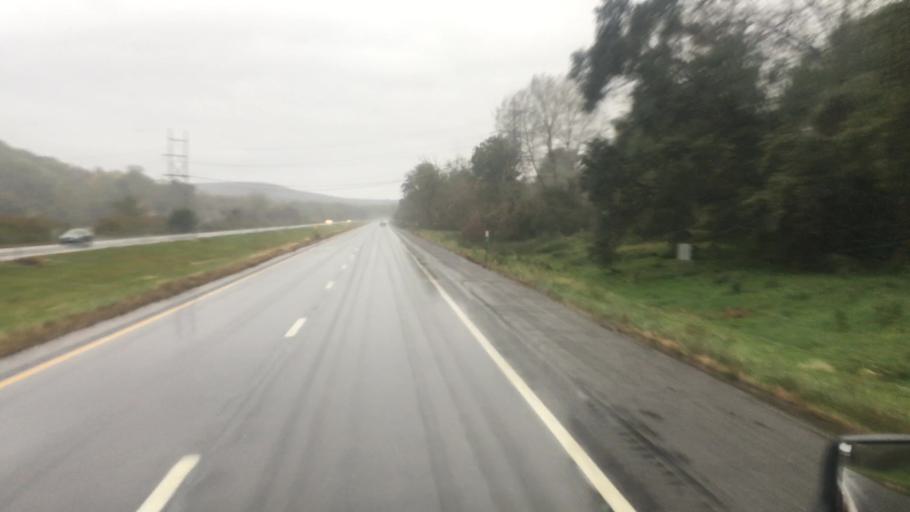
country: US
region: New York
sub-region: Broome County
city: Endicott
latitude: 42.0764
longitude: -76.0837
